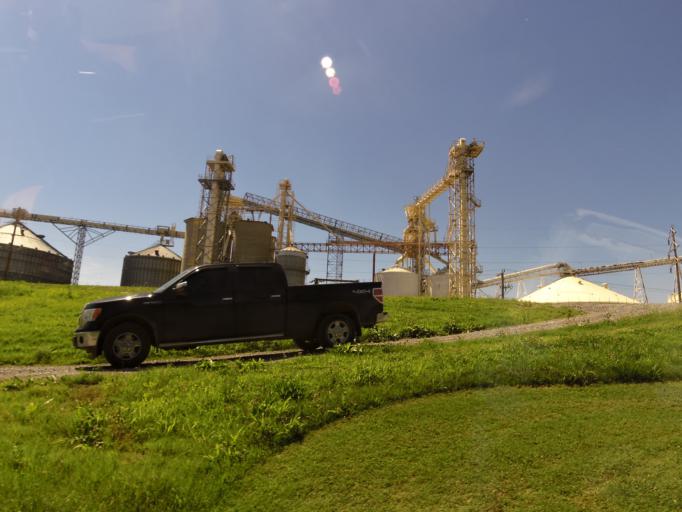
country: US
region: Missouri
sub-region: New Madrid County
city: New Madrid
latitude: 36.5827
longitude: -89.5483
